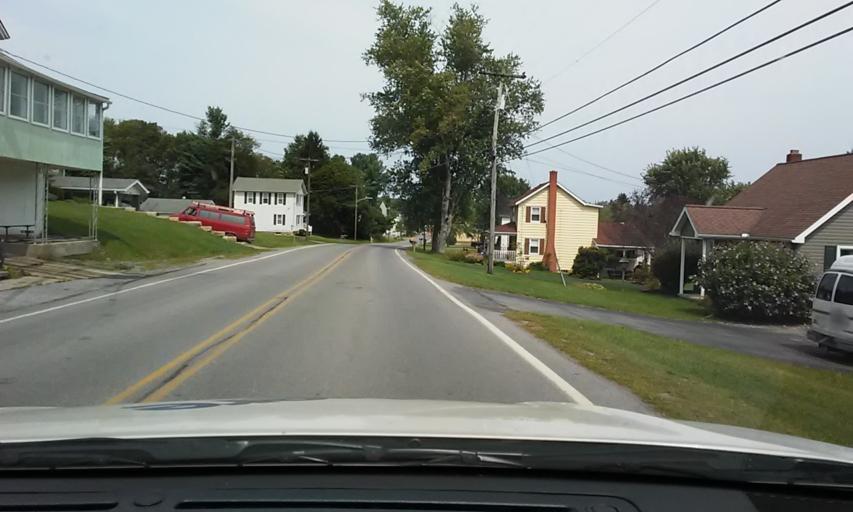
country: US
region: Pennsylvania
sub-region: Elk County
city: Saint Marys
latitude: 41.3583
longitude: -78.6105
